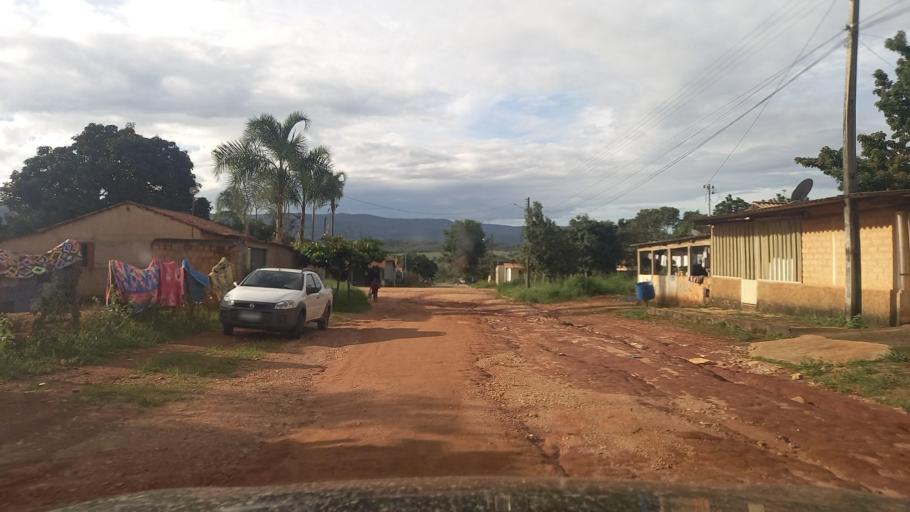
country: BR
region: Goias
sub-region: Cavalcante
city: Cavalcante
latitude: -13.7966
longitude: -47.4427
